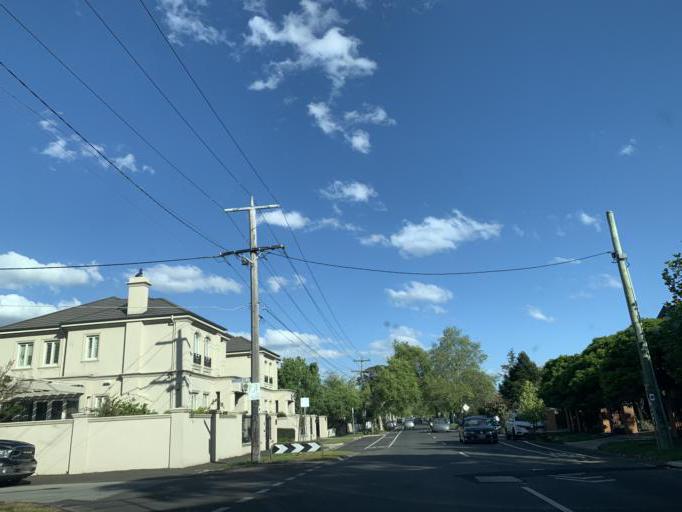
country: AU
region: Victoria
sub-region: Bayside
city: North Brighton
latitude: -37.9078
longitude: 145.0021
